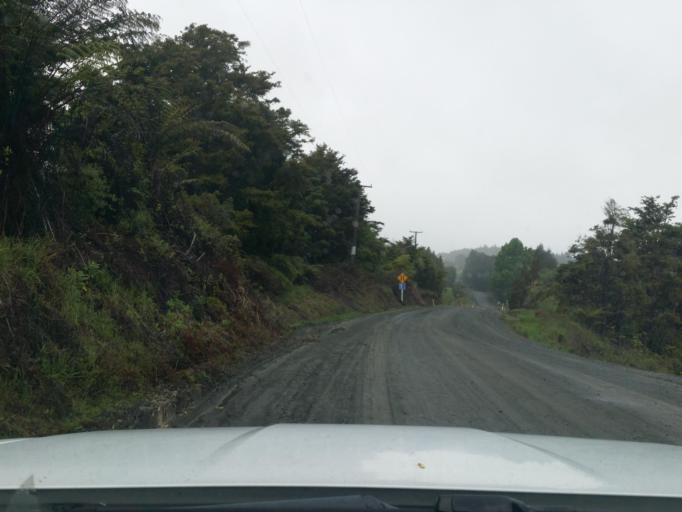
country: NZ
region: Northland
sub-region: Kaipara District
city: Dargaville
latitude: -35.7399
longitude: 173.9081
